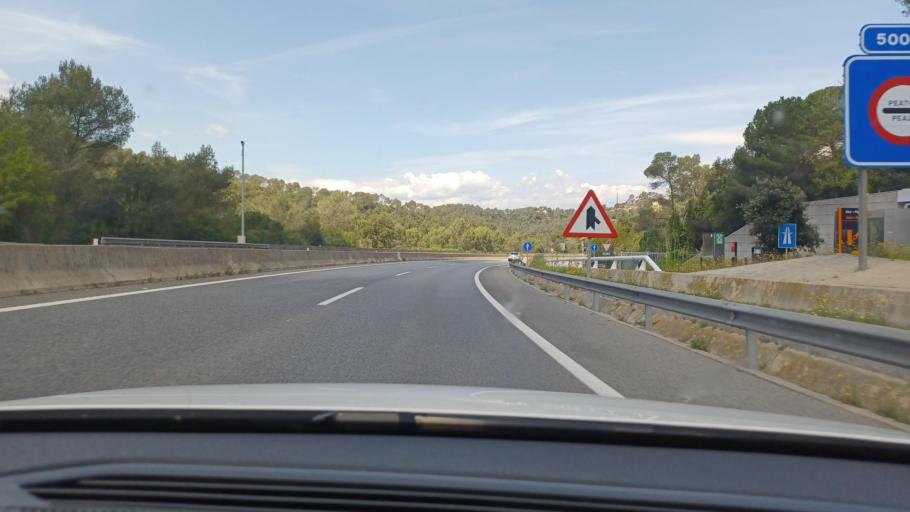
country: ES
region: Catalonia
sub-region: Provincia de Barcelona
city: Sant Cugat del Valles
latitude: 41.4332
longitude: 2.0781
